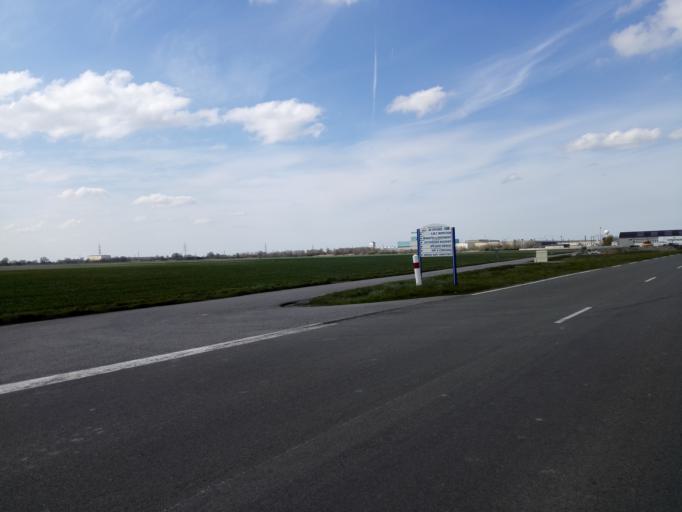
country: FR
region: Nord-Pas-de-Calais
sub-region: Departement du Nord
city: Spycker
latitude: 50.9780
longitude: 2.3081
